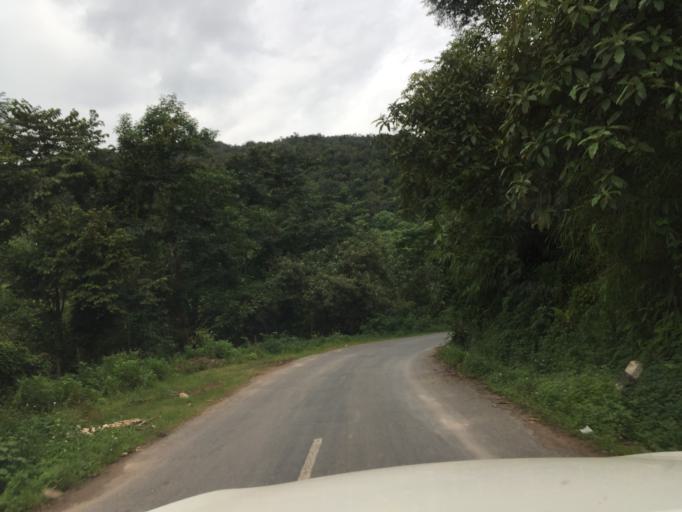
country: LA
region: Phongsali
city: Phongsali
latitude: 21.3435
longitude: 102.0526
